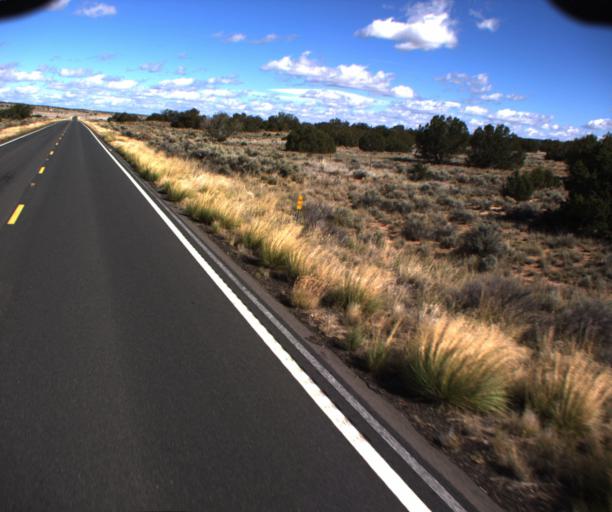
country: US
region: Arizona
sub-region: Apache County
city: Houck
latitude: 34.9098
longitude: -109.2381
